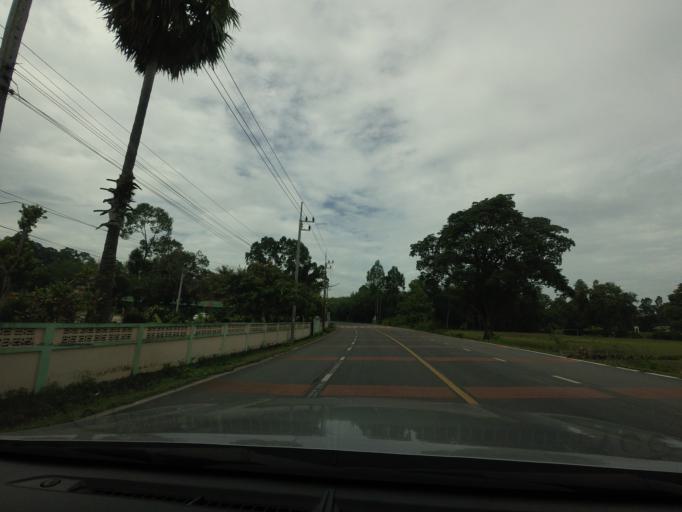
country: TH
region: Nakhon Si Thammarat
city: Phra Phrom
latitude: 8.2872
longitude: 99.9446
